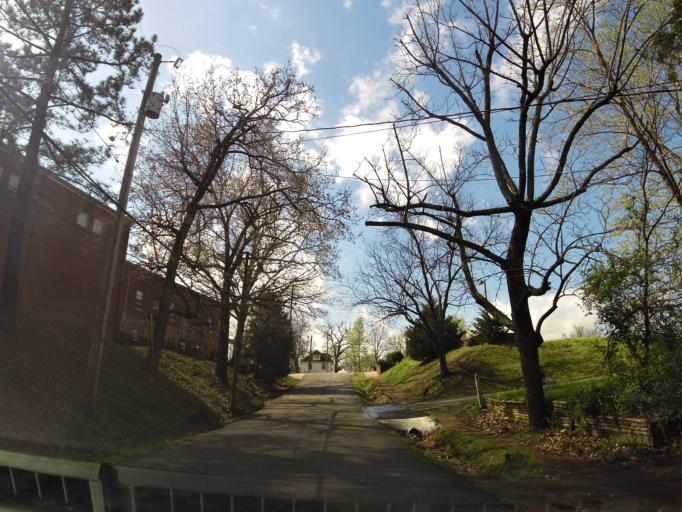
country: US
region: Missouri
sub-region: Butler County
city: Poplar Bluff
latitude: 36.7629
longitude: -90.3961
